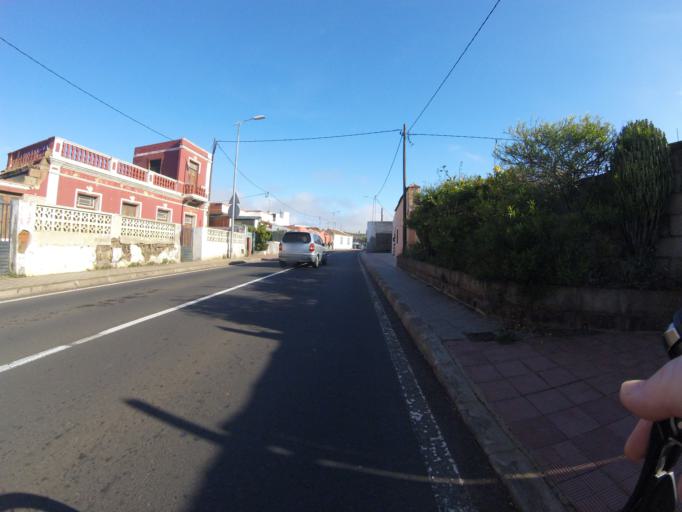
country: ES
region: Canary Islands
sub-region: Provincia de Santa Cruz de Tenerife
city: La Laguna
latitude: 28.4620
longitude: -16.3159
